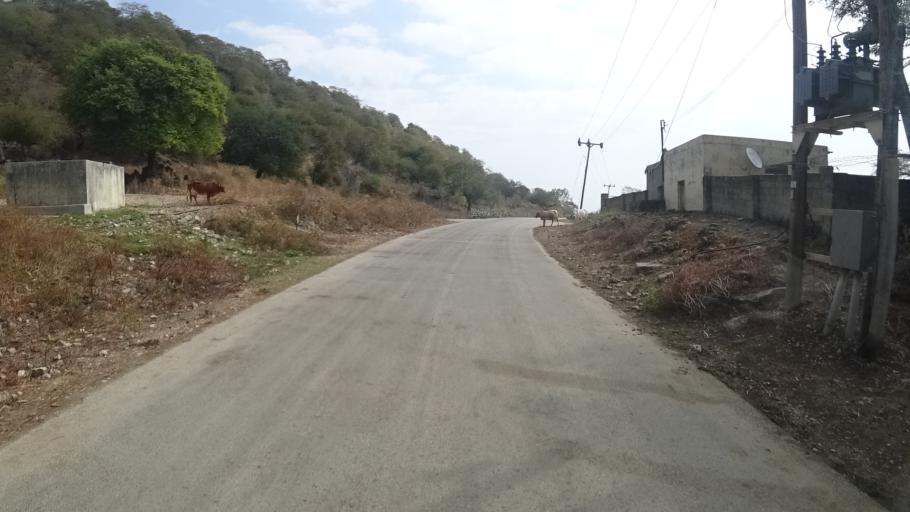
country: YE
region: Al Mahrah
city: Hawf
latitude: 16.7101
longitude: 53.2363
